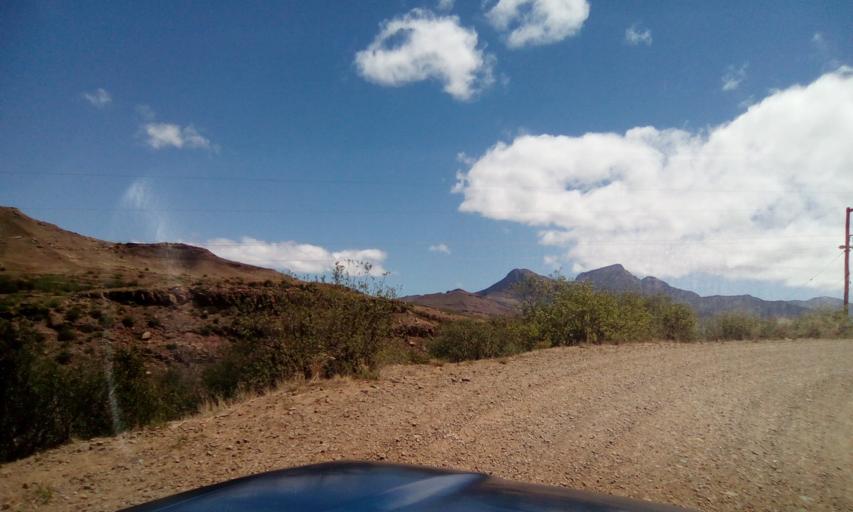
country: LS
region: Qacha's Nek
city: Qacha's Nek
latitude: -30.0693
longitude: 28.6228
